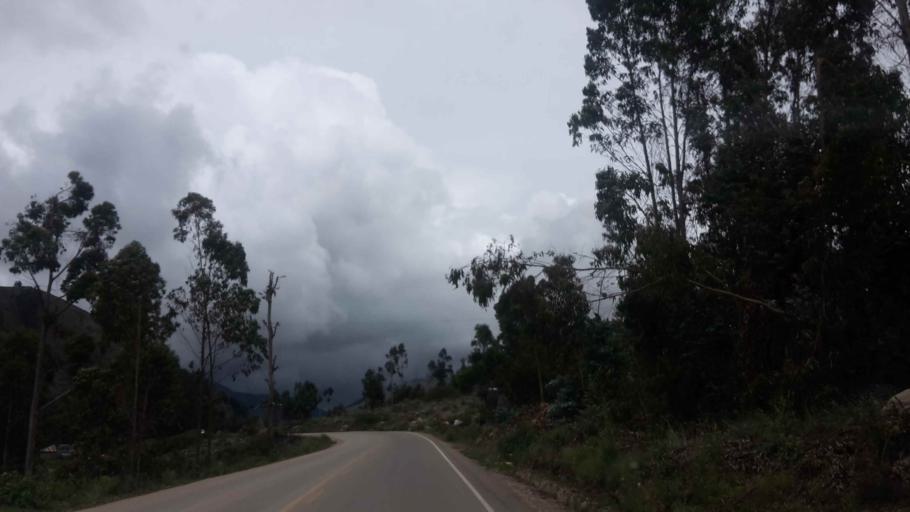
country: BO
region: Cochabamba
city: Arani
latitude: -17.4770
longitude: -65.5122
